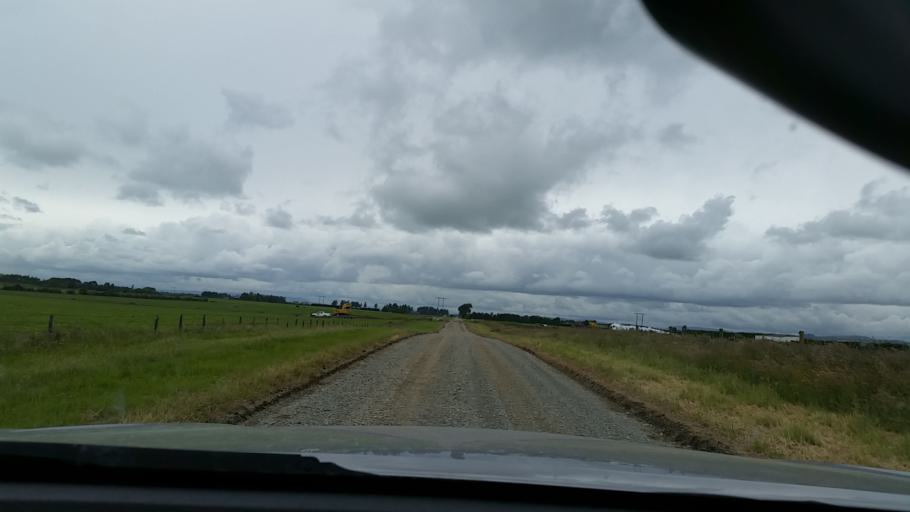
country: NZ
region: Southland
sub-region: Southland District
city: Winton
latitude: -46.2615
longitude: 168.3673
